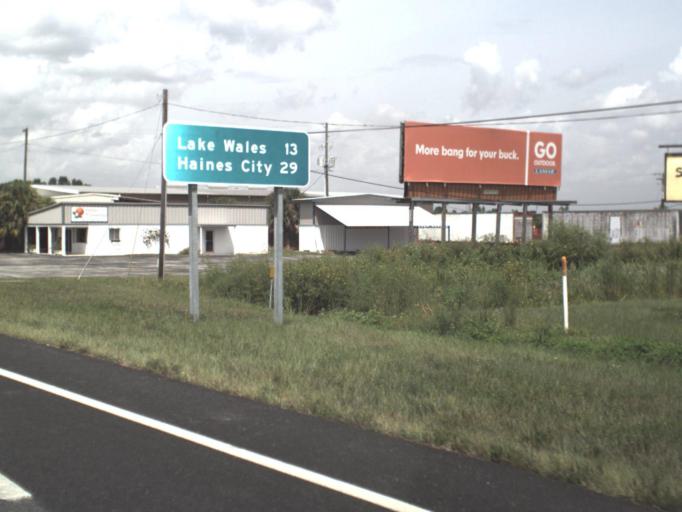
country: US
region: Florida
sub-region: Polk County
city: Frostproof
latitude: 27.7350
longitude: -81.5734
